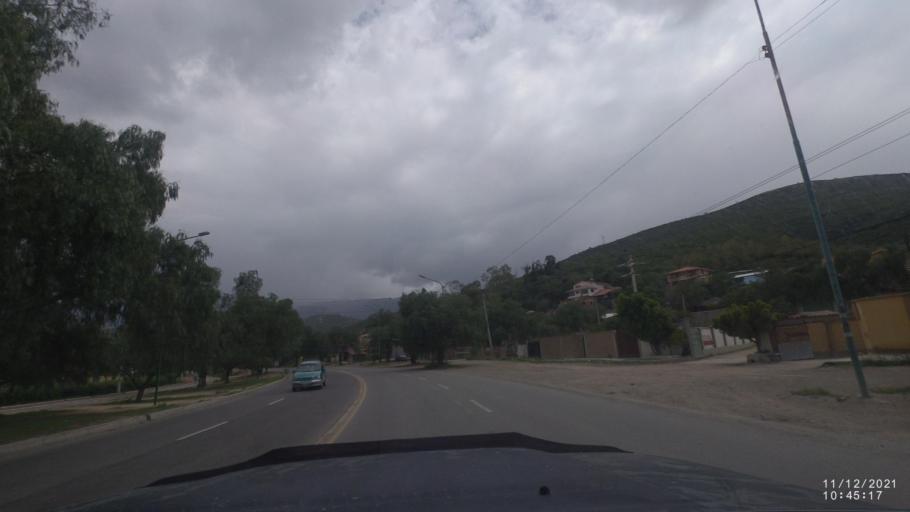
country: BO
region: Cochabamba
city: Cochabamba
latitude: -17.4161
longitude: -66.1262
